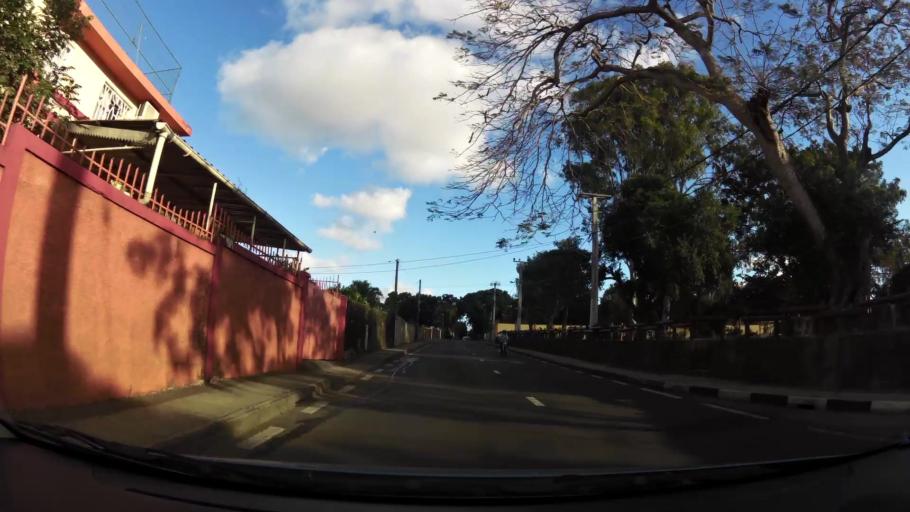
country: MU
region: Moka
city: Moka
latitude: -20.2267
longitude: 57.4636
